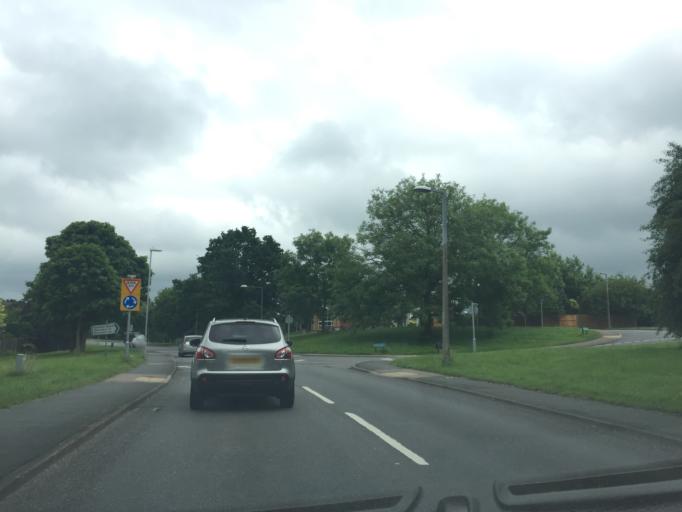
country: GB
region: England
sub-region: Essex
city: Harlow
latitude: 51.7468
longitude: 0.0856
